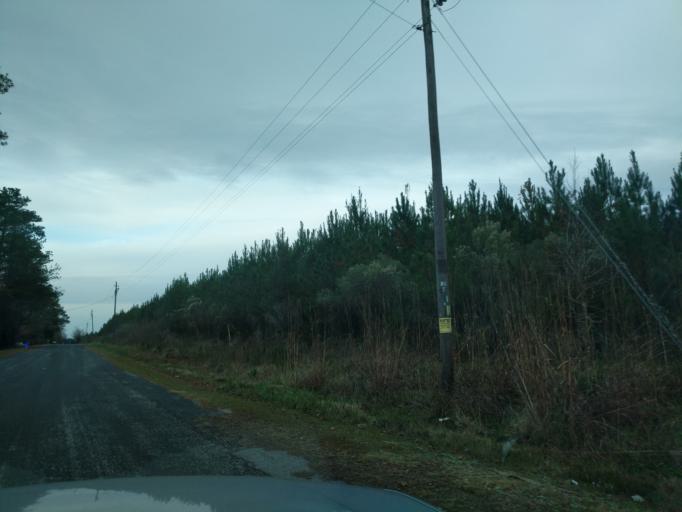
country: US
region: South Carolina
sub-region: Laurens County
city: Laurens
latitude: 34.3401
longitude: -81.9919
